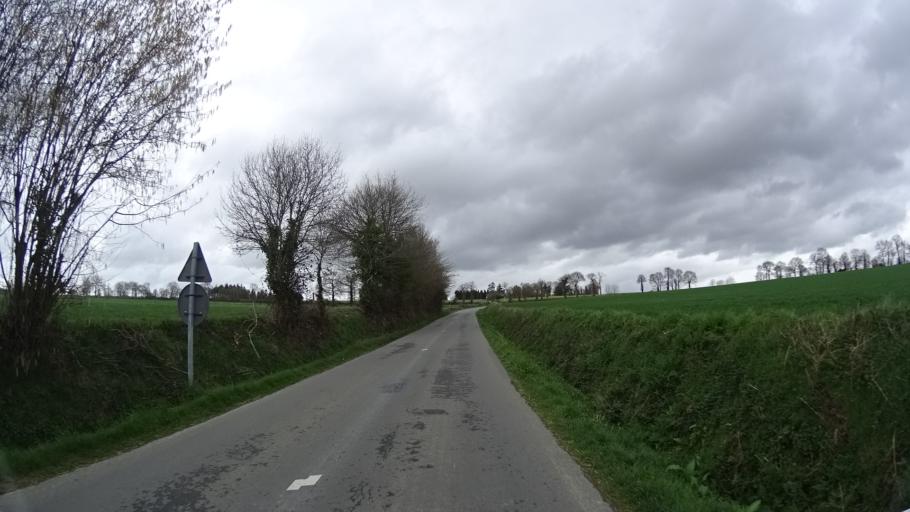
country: FR
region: Brittany
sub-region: Departement d'Ille-et-Vilaine
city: Saint-Gilles
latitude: 48.1717
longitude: -1.8291
